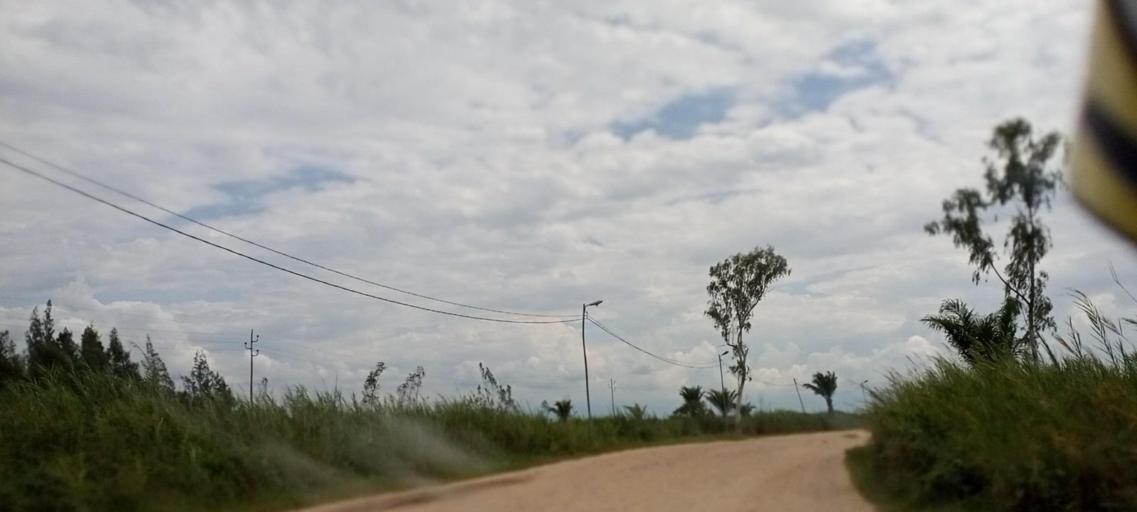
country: CD
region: South Kivu
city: Uvira
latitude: -3.3393
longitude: 29.2041
